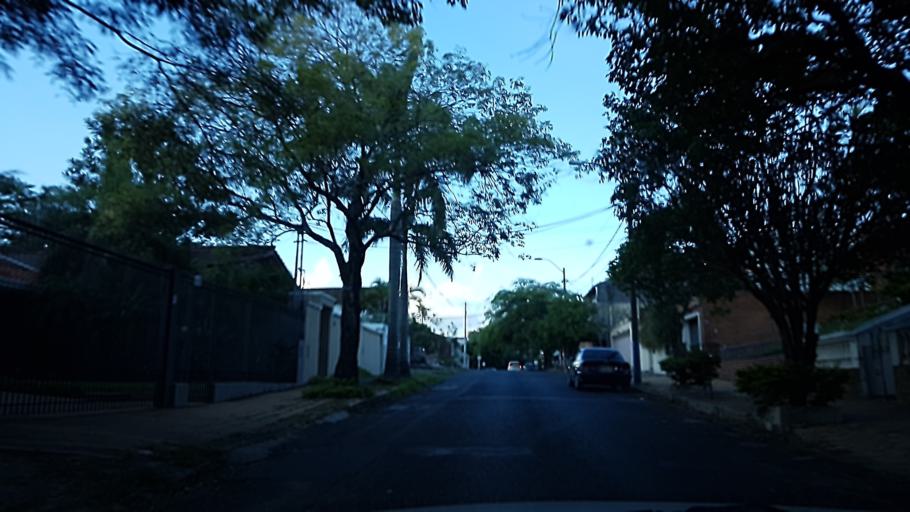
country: PY
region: Asuncion
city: Asuncion
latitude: -25.2860
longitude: -57.6062
